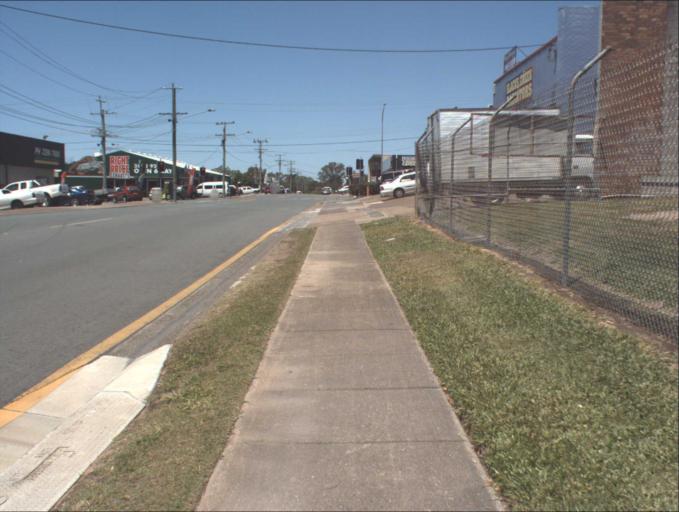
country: AU
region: Queensland
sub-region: Logan
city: Springwood
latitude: -27.6212
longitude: 153.1221
